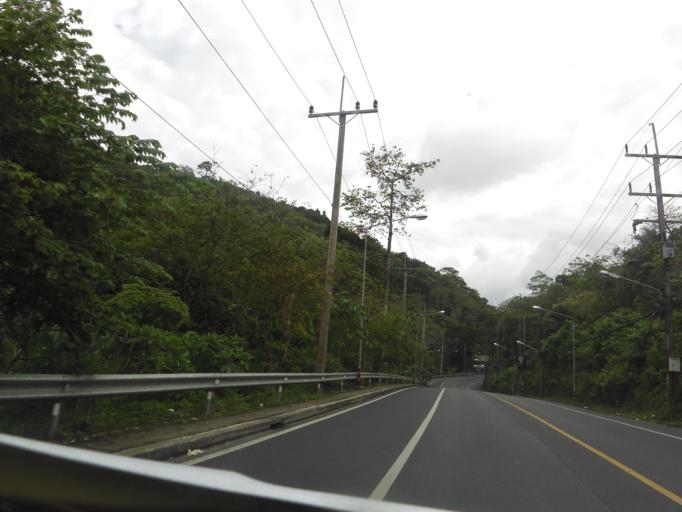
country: TH
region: Phuket
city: Ban Karon
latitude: 7.8685
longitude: 98.2854
